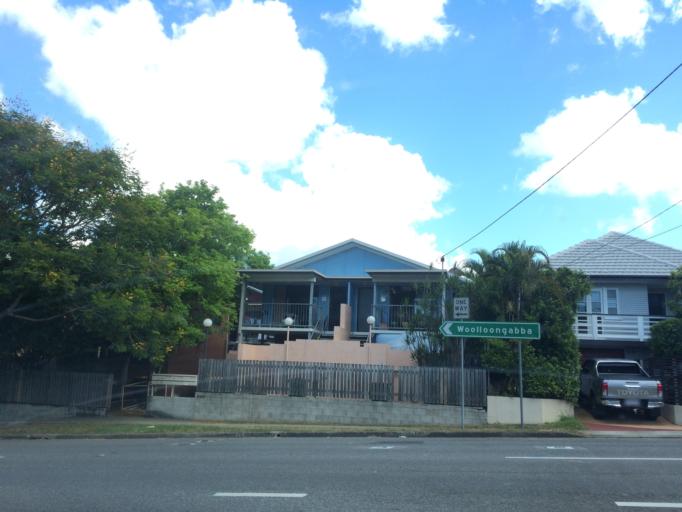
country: AU
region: Queensland
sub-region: Brisbane
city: Woolloongabba
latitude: -27.4858
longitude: 153.0456
